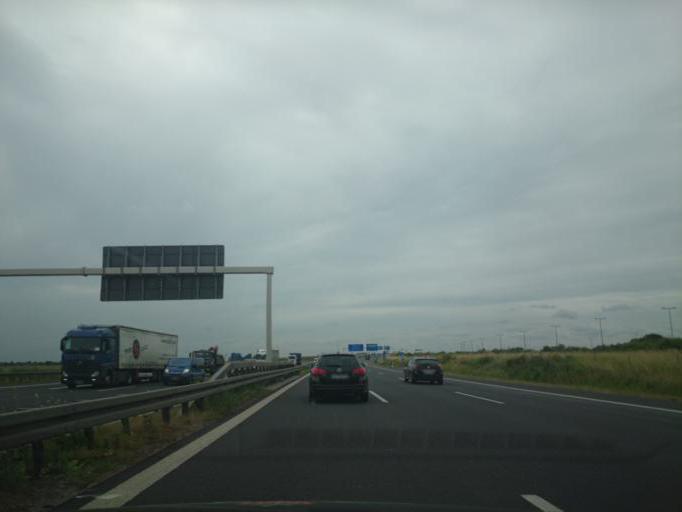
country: DE
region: Brandenburg
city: Schonefeld
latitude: 52.3832
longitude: 13.5366
